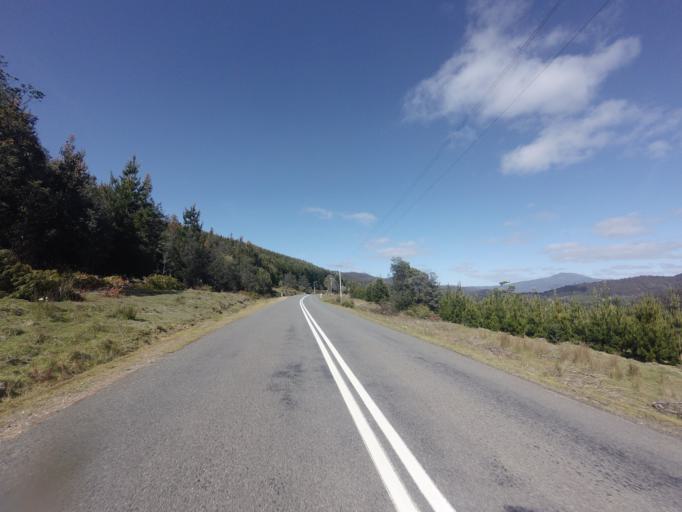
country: AU
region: Tasmania
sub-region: Derwent Valley
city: New Norfolk
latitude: -42.7424
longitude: 146.6573
